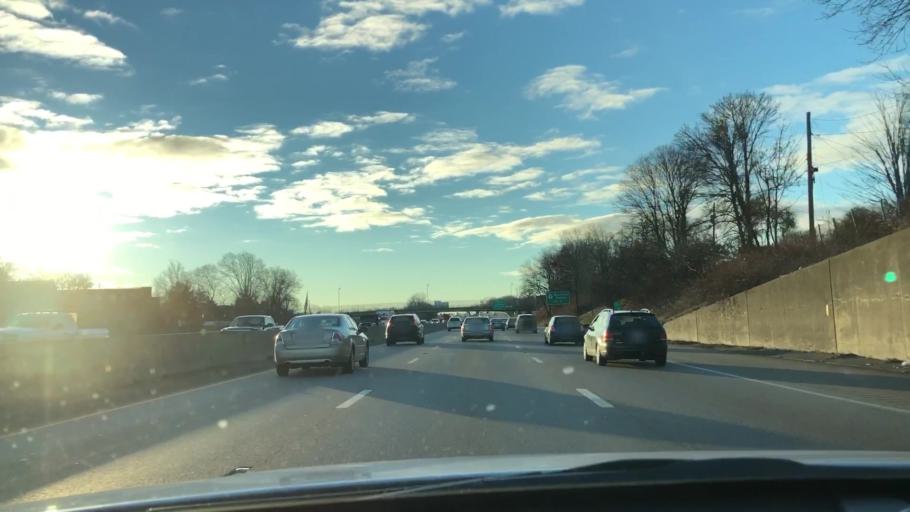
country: US
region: Massachusetts
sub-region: Norfolk County
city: Braintree
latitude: 42.2244
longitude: -71.0037
